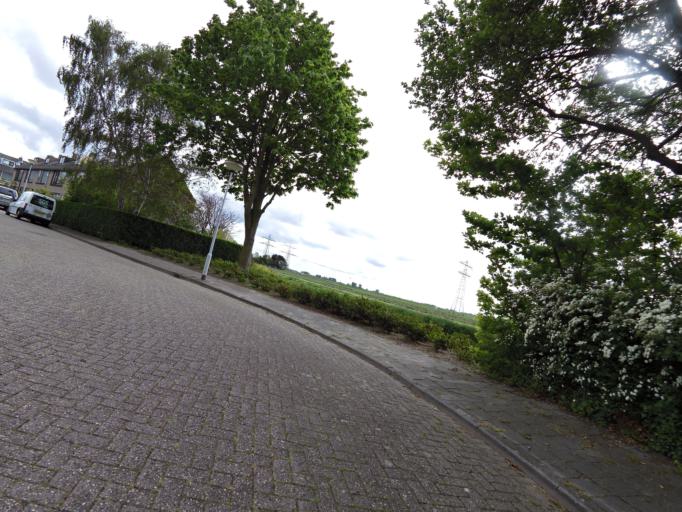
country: NL
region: South Holland
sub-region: Gemeente Brielle
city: Brielle
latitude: 51.8929
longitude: 4.1562
